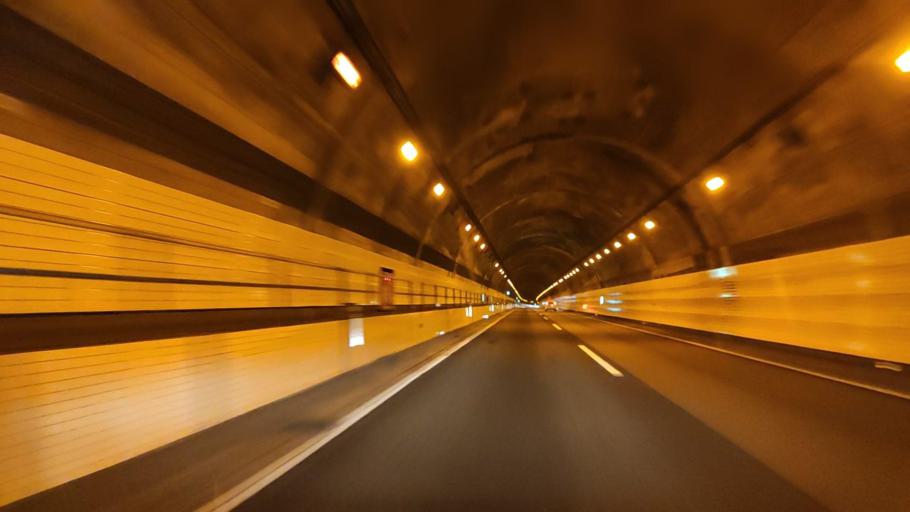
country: JP
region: Iwate
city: Ichinoseki
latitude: 38.9906
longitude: 141.0992
